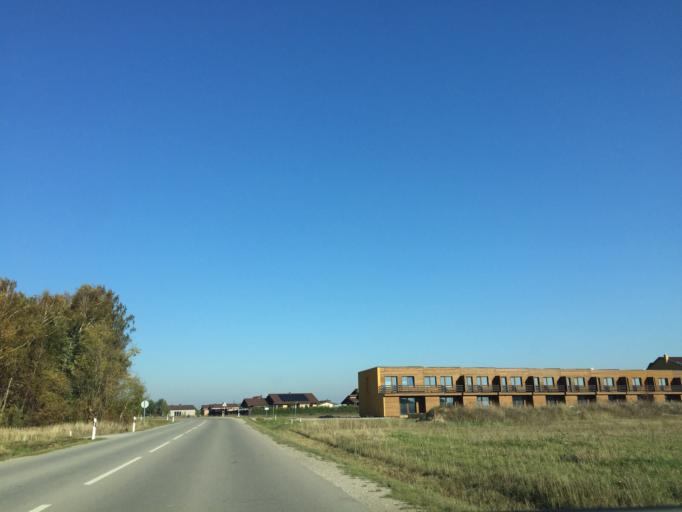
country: LT
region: Klaipedos apskritis
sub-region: Klaipeda
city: Klaipeda
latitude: 55.7604
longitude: 21.1955
